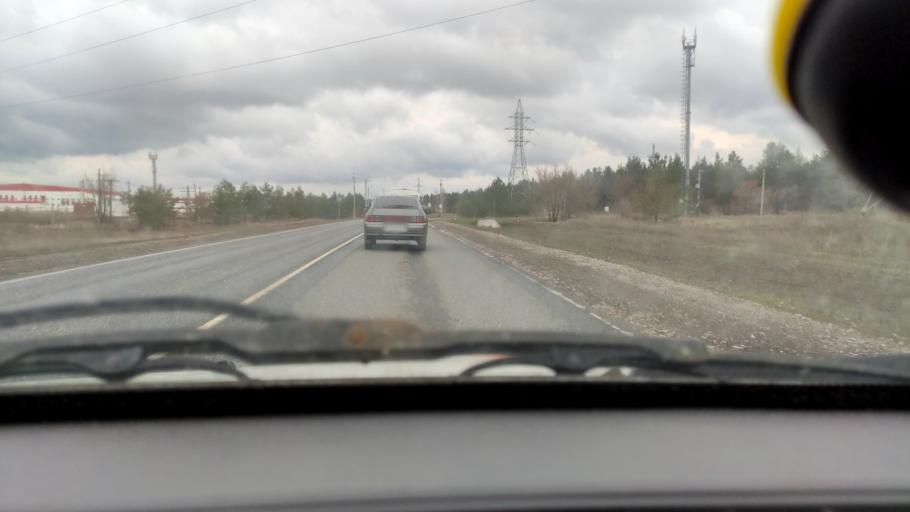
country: RU
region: Samara
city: Zhigulevsk
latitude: 53.5616
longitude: 49.5413
